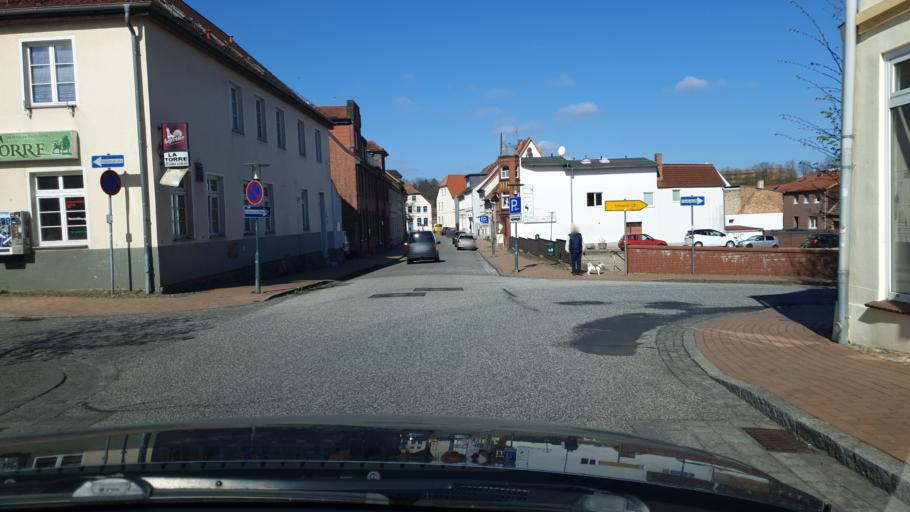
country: DE
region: Mecklenburg-Vorpommern
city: Crivitz
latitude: 53.5776
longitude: 11.6497
